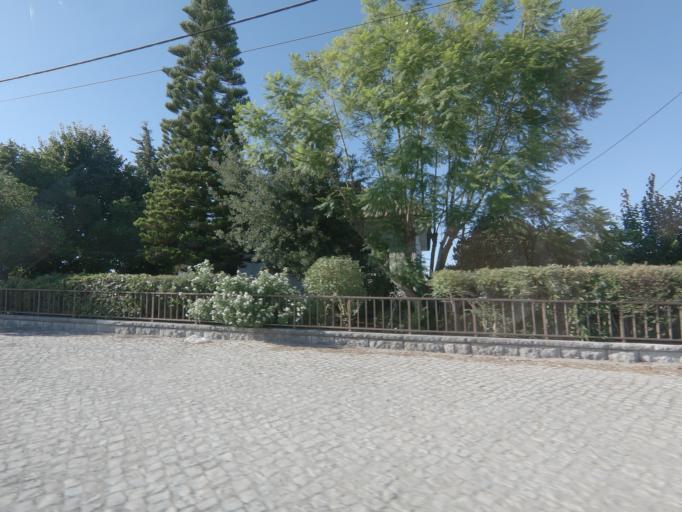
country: PT
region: Setubal
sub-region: Palmela
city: Quinta do Anjo
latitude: 38.5677
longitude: -8.9315
